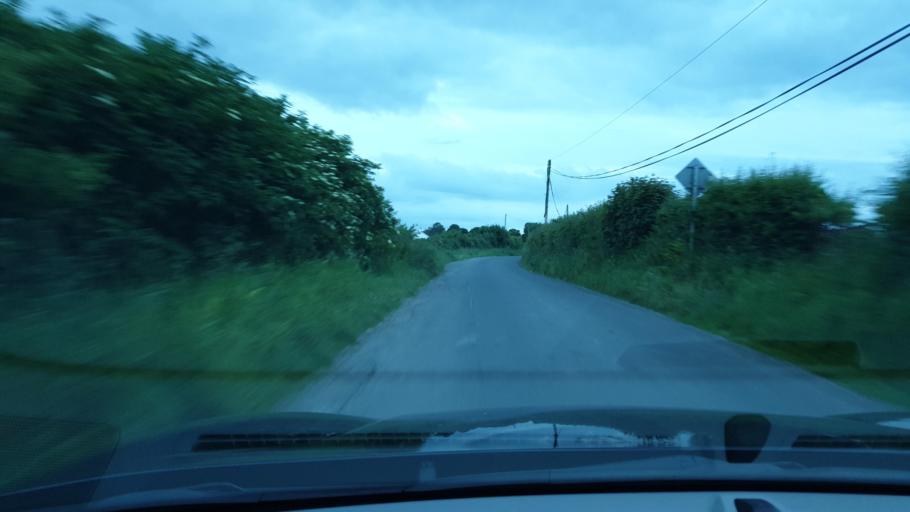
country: IE
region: Leinster
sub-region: An Mhi
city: Duleek
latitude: 53.6049
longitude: -6.3749
